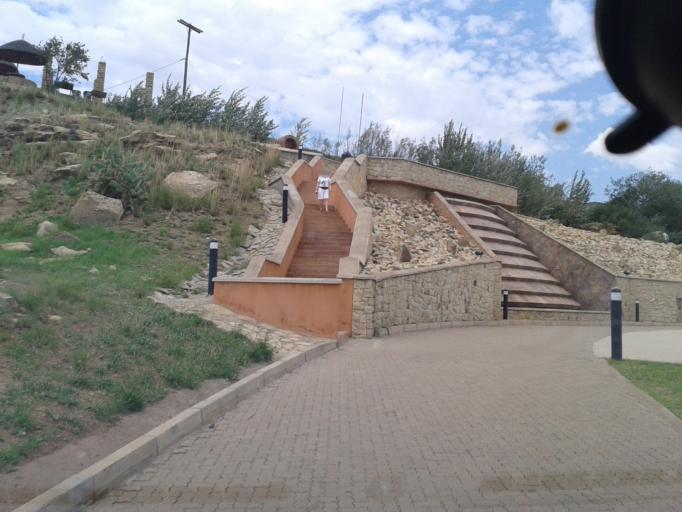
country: LS
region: Maseru
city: Maseru
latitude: -29.3460
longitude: 27.6634
